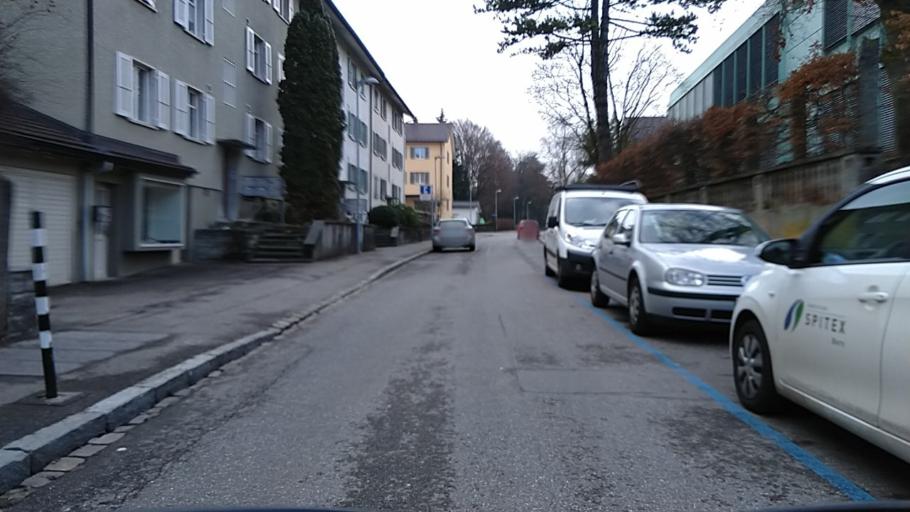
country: CH
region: Bern
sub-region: Bern-Mittelland District
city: Koniz
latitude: 46.9426
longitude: 7.3868
